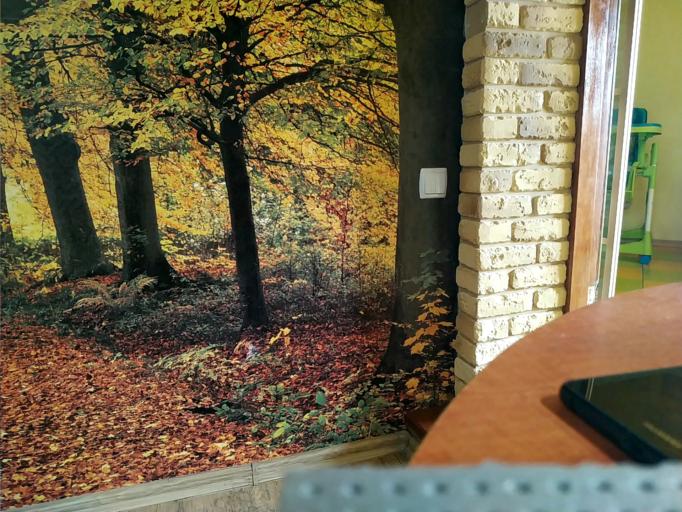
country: RU
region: Tverskaya
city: Kalashnikovo
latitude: 57.3036
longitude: 35.1080
